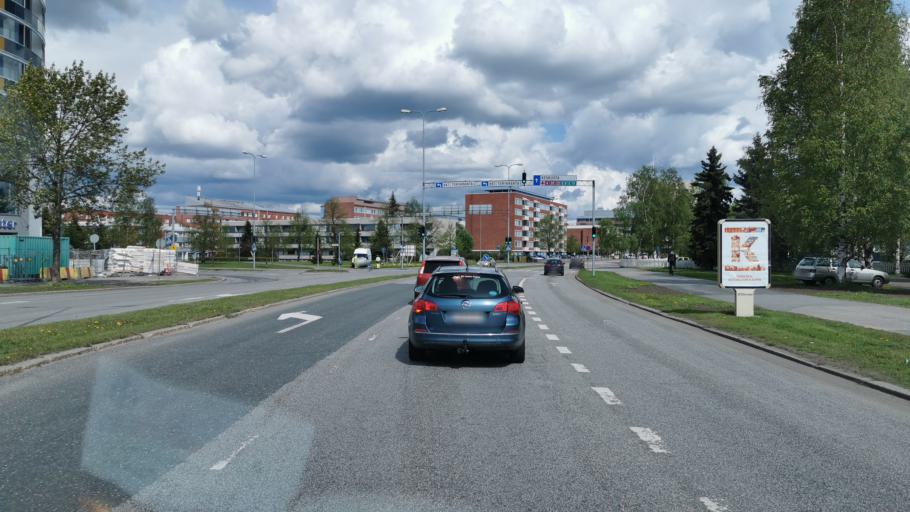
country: FI
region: Northern Ostrobothnia
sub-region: Oulu
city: Oulu
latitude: 65.0032
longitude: 25.4637
